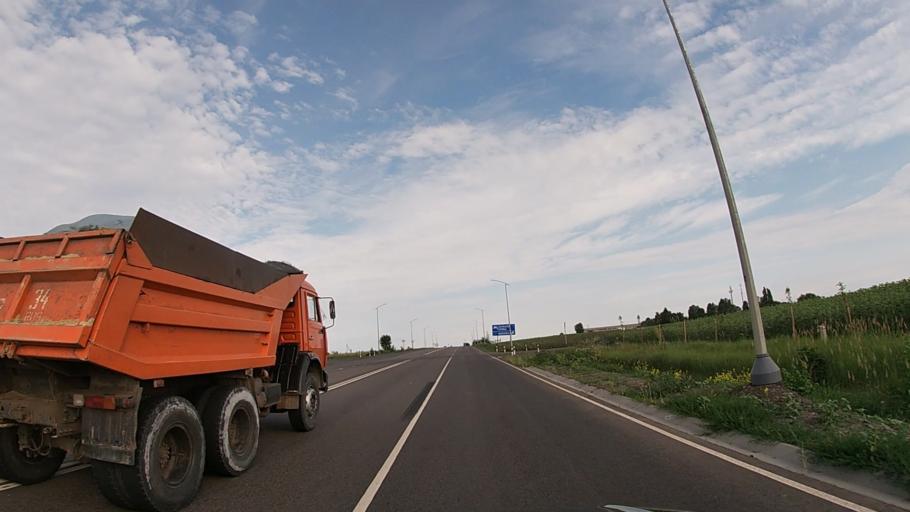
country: RU
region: Belgorod
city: Severnyy
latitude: 50.6716
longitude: 36.4820
